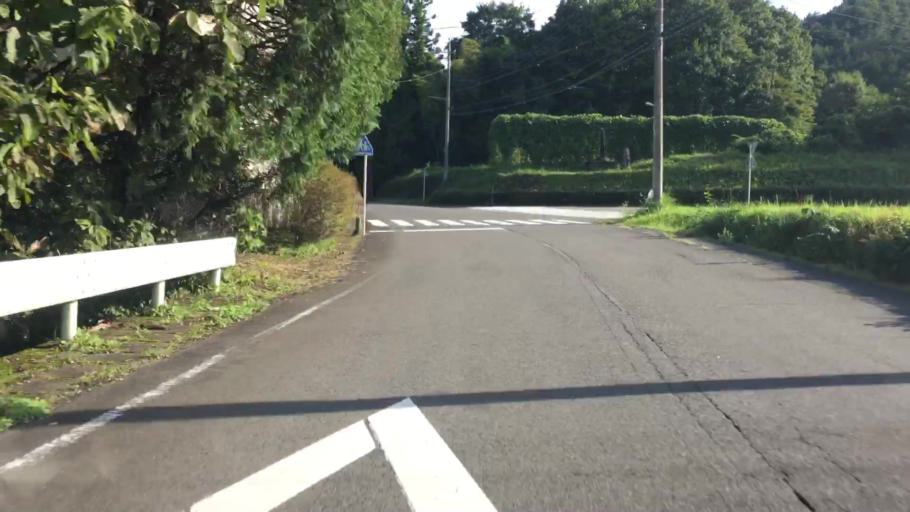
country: JP
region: Tochigi
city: Imaichi
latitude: 36.7593
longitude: 139.6830
